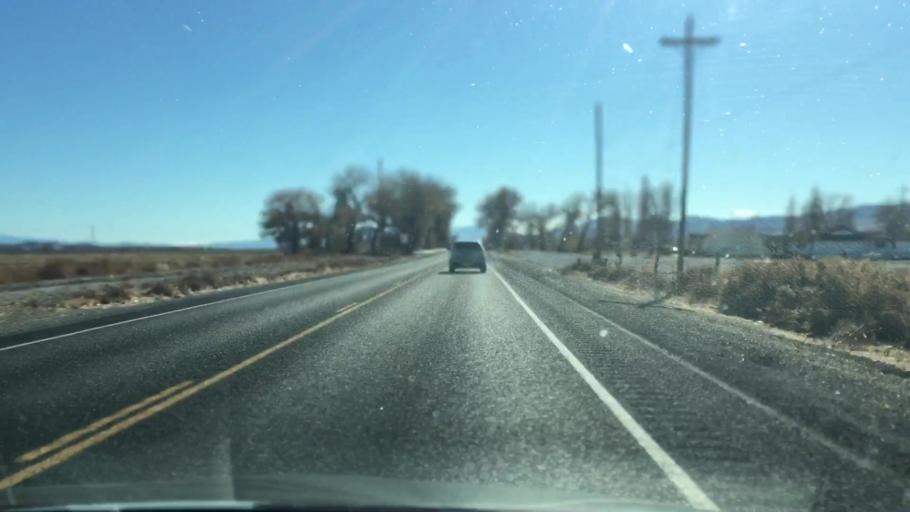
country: US
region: Nevada
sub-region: Lyon County
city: Yerington
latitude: 39.0522
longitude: -119.1814
